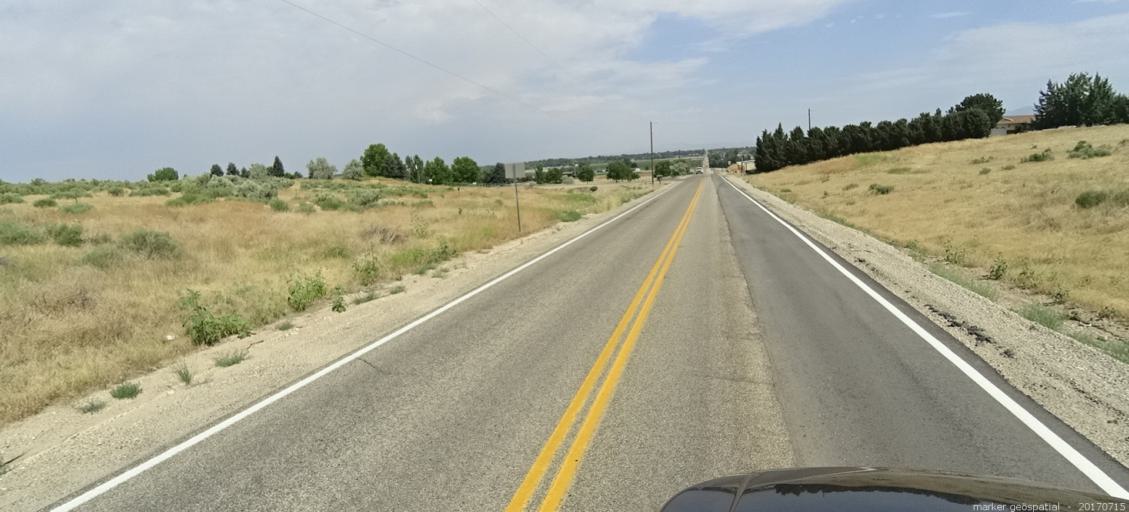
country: US
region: Idaho
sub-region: Ada County
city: Garden City
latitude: 43.5237
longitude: -116.2742
